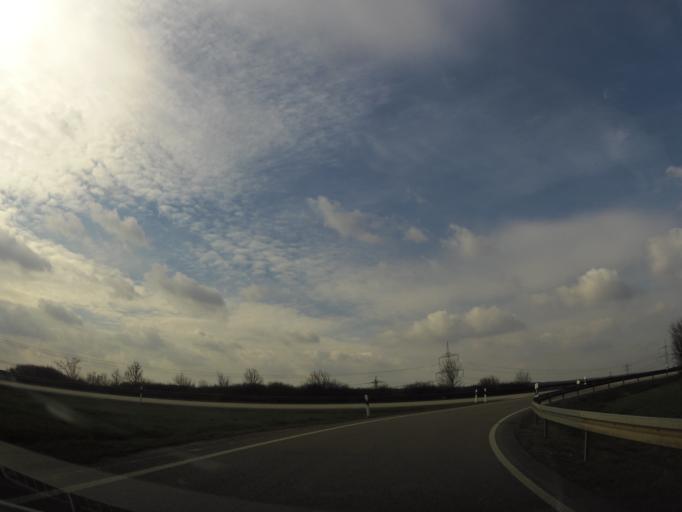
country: DE
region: Thuringia
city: Troistedt
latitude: 50.9500
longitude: 11.2437
